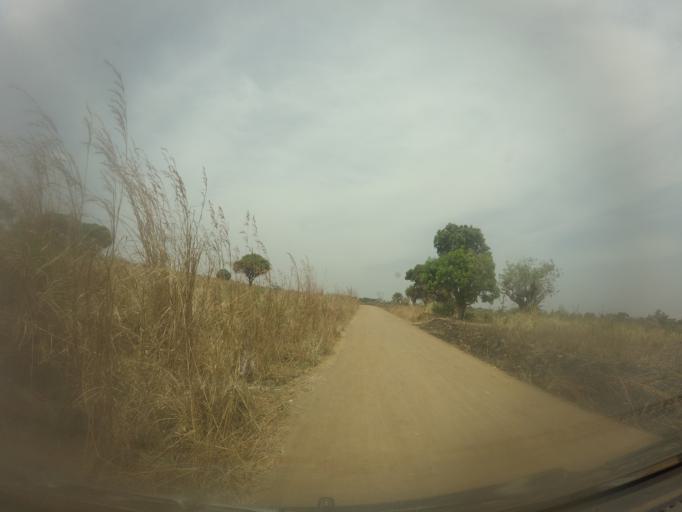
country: UG
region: Northern Region
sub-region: Zombo District
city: Zombo
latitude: 2.7657
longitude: 31.0342
